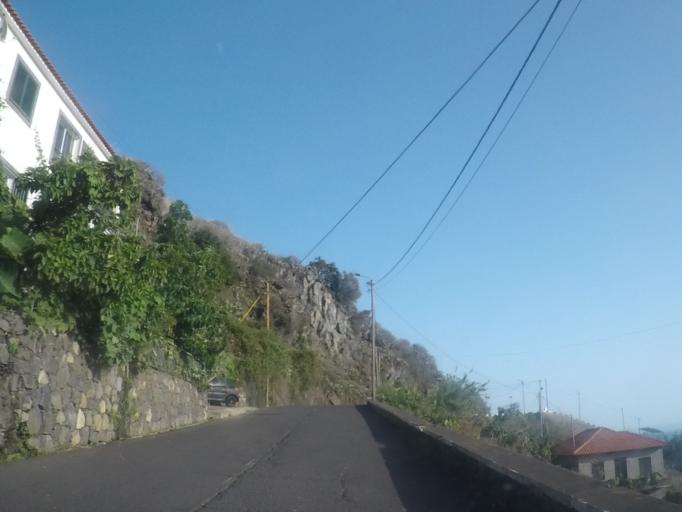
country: PT
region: Madeira
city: Ribeira Brava
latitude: 32.6789
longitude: -17.0716
